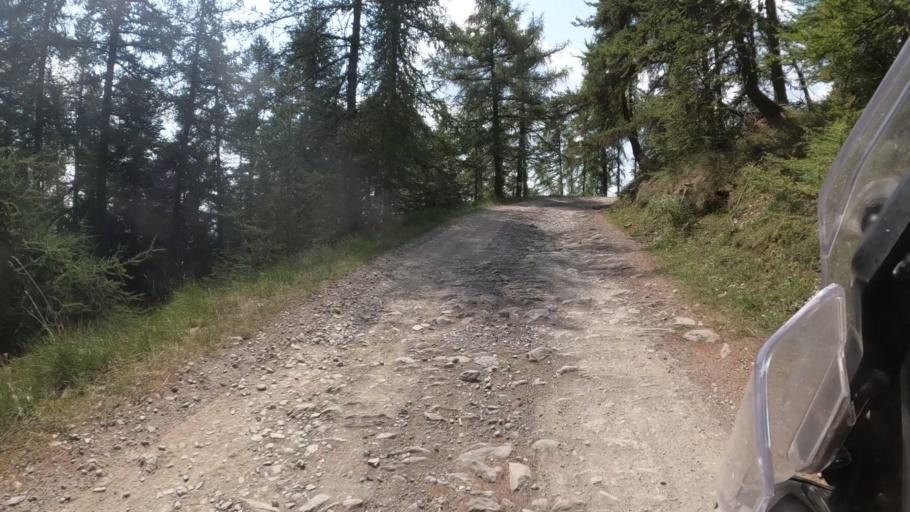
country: IT
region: Piedmont
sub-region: Provincia di Cuneo
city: Briga Alta
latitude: 44.0298
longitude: 7.6755
